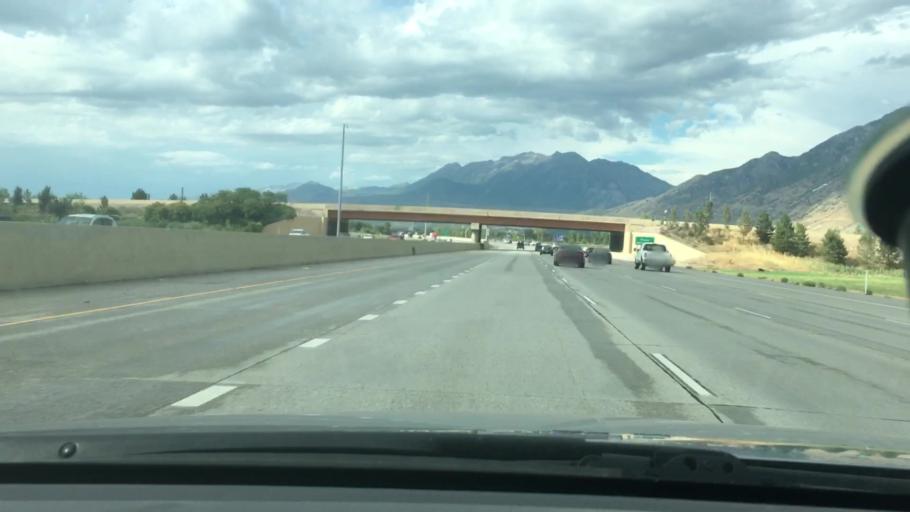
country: US
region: Utah
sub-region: Utah County
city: Springville
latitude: 40.1859
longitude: -111.6464
